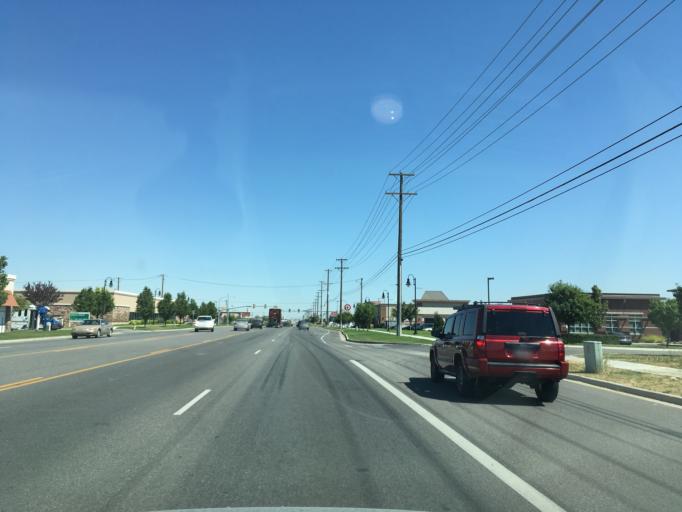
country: US
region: Utah
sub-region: Salt Lake County
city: West Valley City
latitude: 40.7092
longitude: -112.0248
